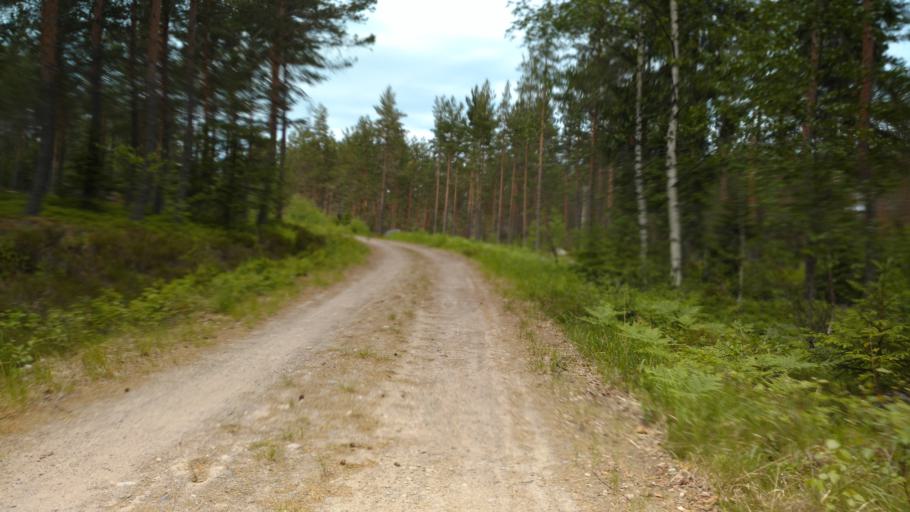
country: FI
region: Uusimaa
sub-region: Raaseporin
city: Pohja
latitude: 60.1138
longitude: 23.5543
